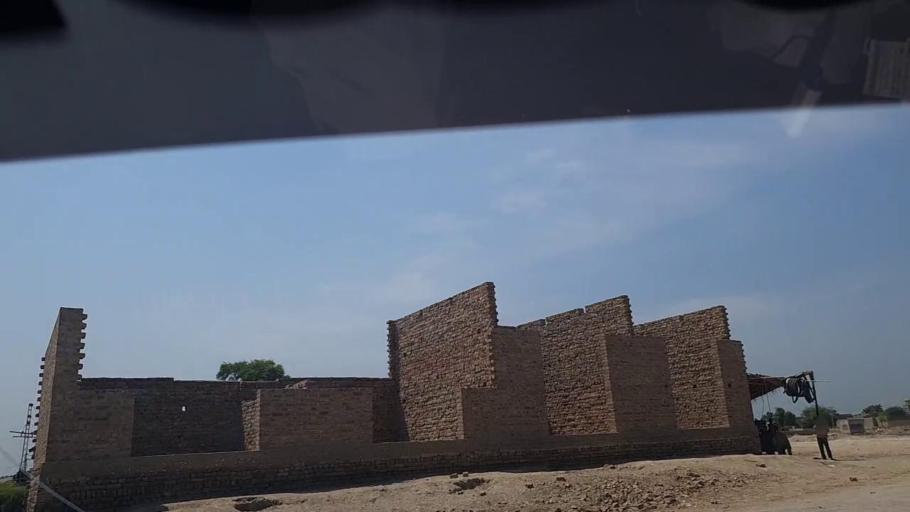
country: PK
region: Sindh
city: Thul
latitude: 28.1779
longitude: 68.7289
